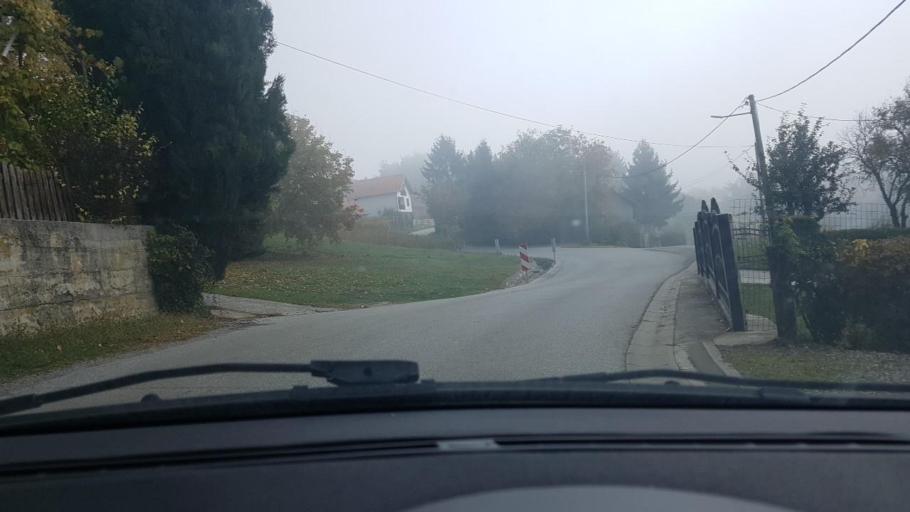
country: HR
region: Varazdinska
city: Lepoglava
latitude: 46.1570
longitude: 16.0254
